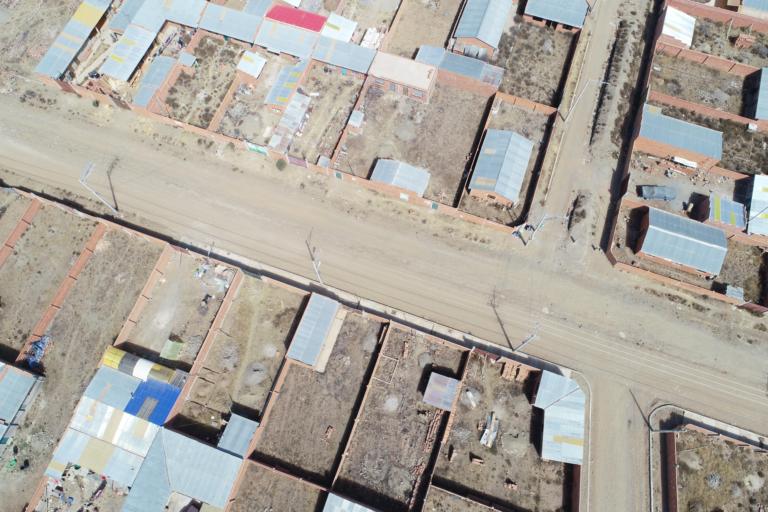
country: BO
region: La Paz
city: La Paz
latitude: -16.5923
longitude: -68.2109
